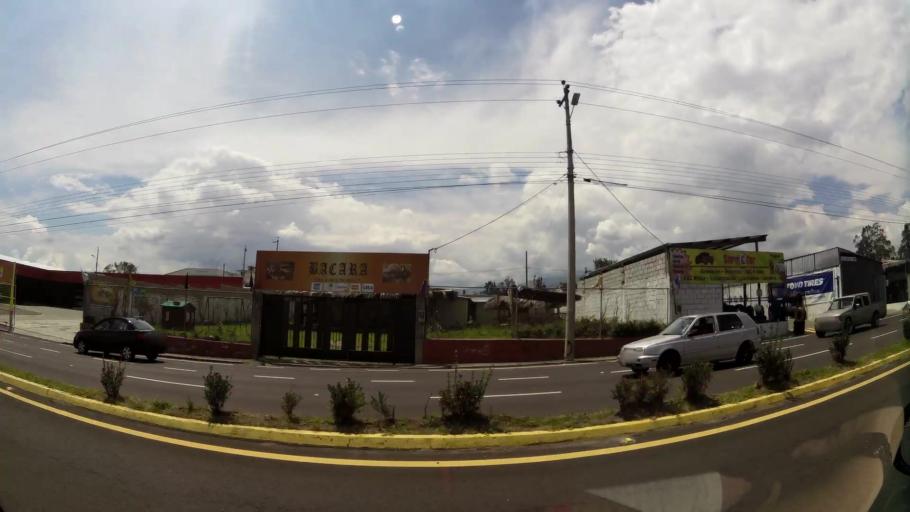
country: EC
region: Pichincha
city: Sangolqui
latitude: -0.2068
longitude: -78.3668
